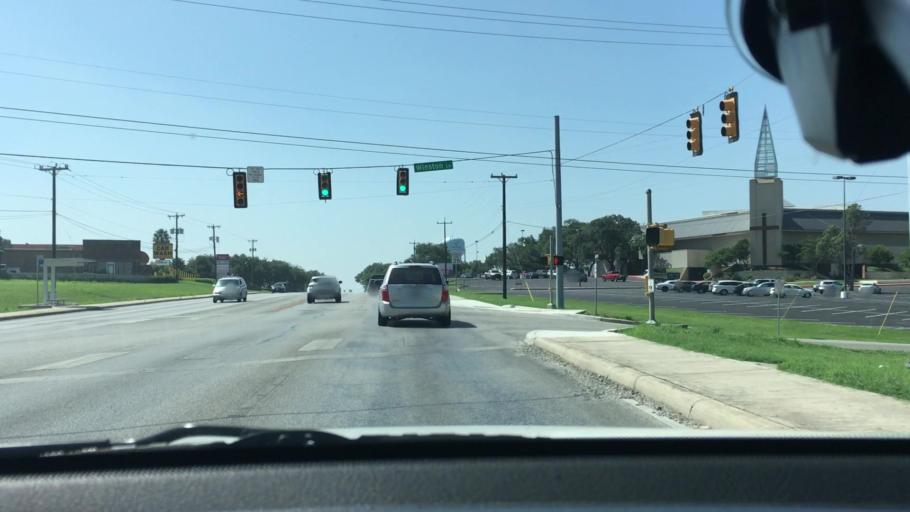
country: US
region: Texas
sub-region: Bexar County
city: Castle Hills
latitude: 29.5365
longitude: -98.5255
